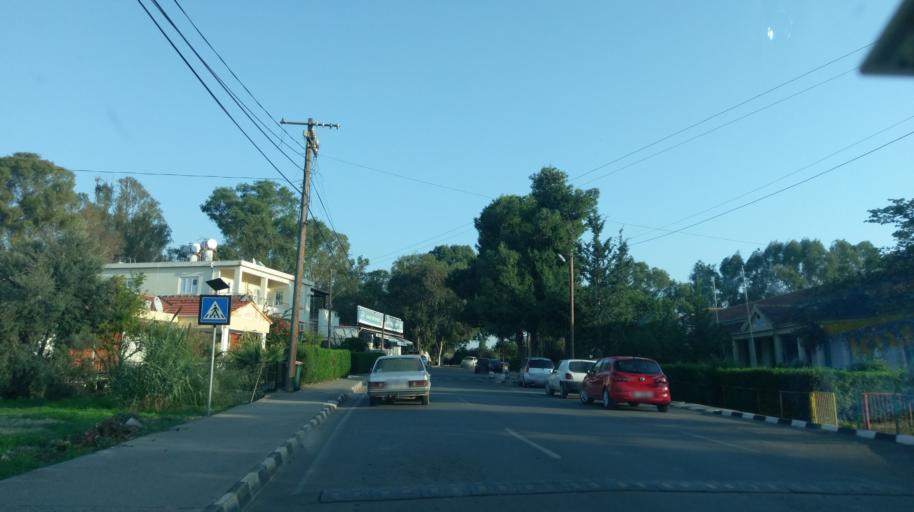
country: CY
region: Lefkosia
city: Astromeritis
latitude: 35.1660
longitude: 33.0115
